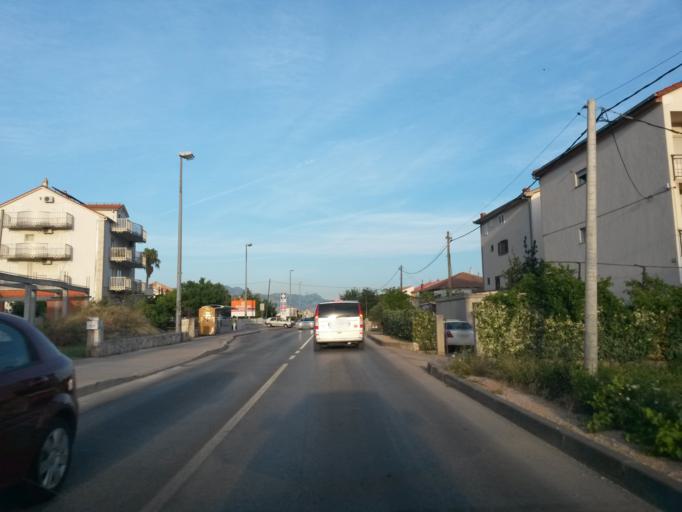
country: HR
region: Splitsko-Dalmatinska
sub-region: Grad Split
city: Split
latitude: 43.5520
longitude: 16.3756
